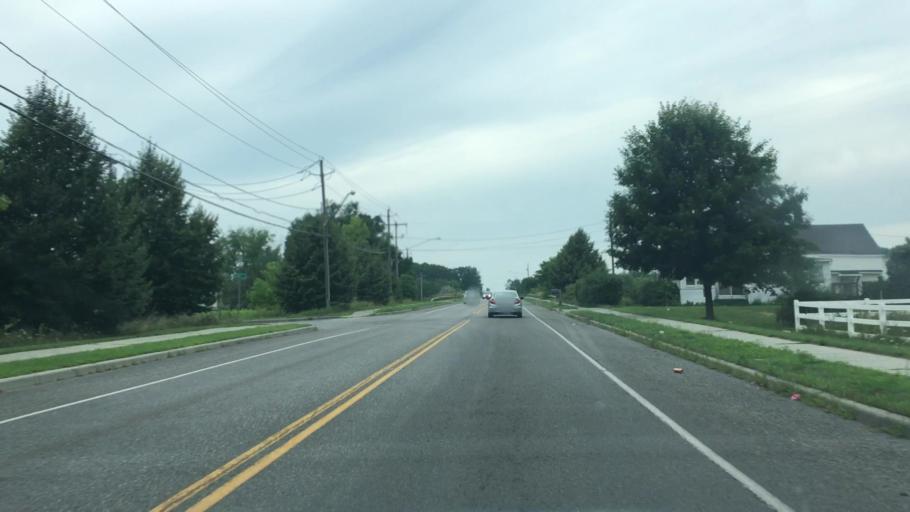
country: US
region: New York
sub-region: Clinton County
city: Plattsburgh West
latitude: 44.6872
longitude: -73.4866
